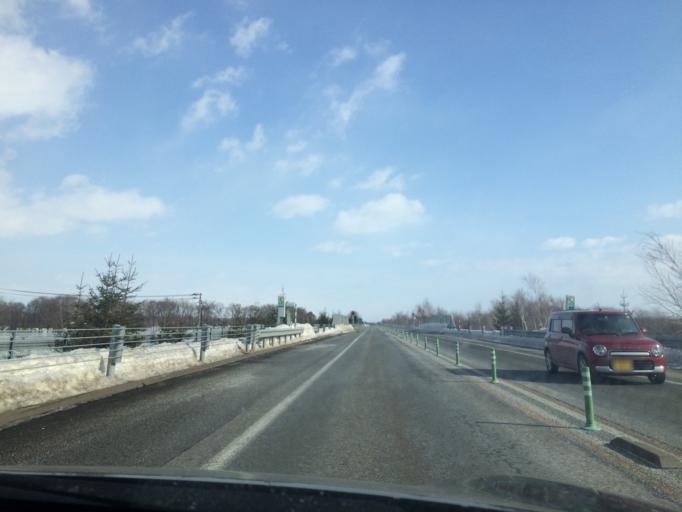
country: JP
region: Hokkaido
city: Chitose
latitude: 42.8644
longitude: 141.6088
